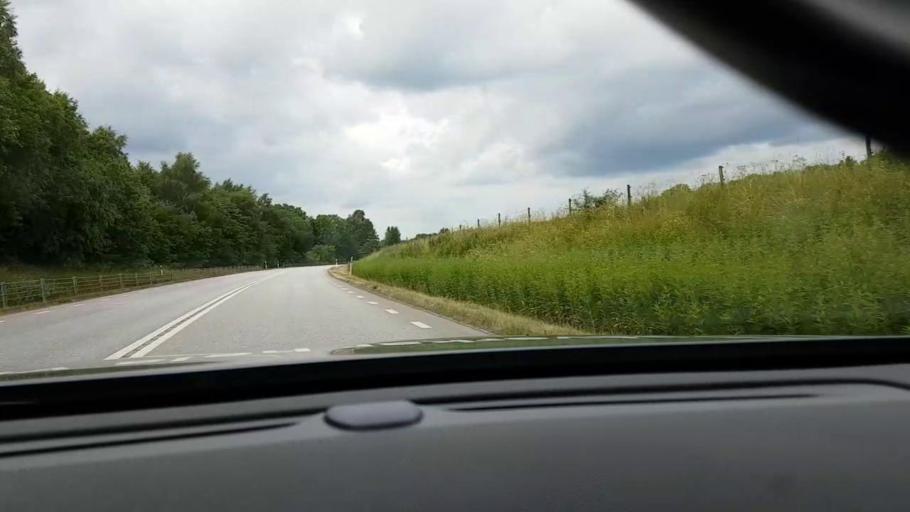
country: SE
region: Skane
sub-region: Horby Kommun
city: Hoerby
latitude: 55.8745
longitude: 13.6324
